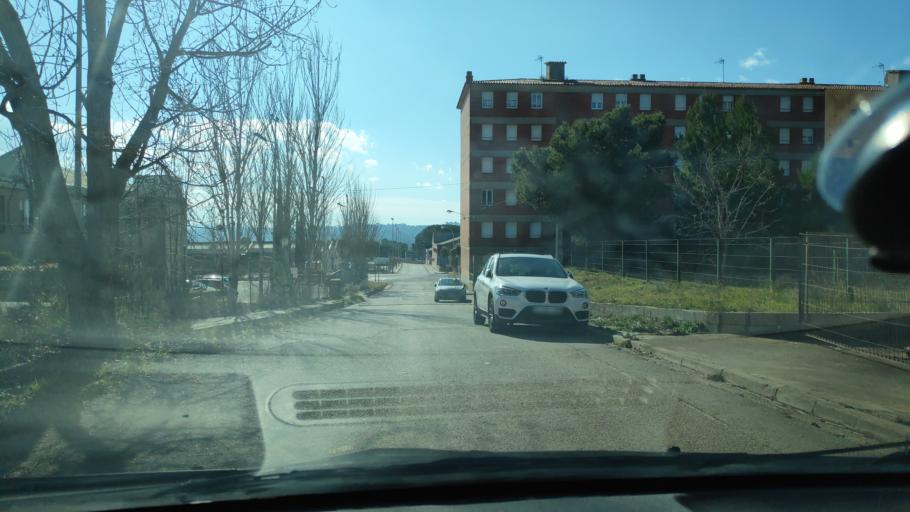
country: ES
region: Catalonia
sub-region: Provincia de Barcelona
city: Sant Quirze del Valles
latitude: 41.5557
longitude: 2.0594
